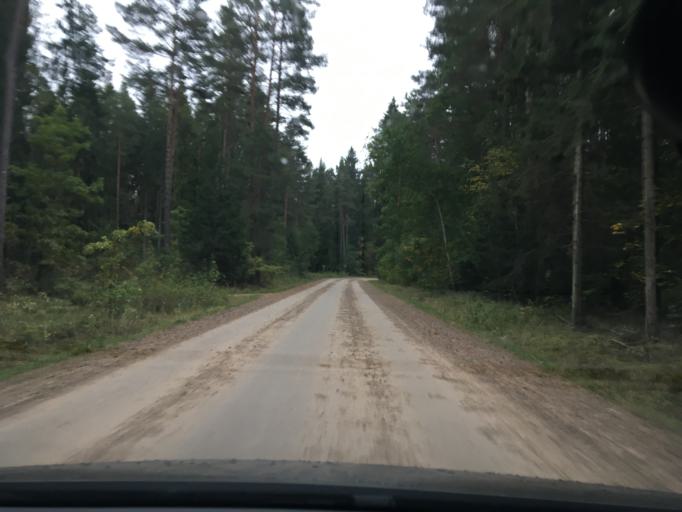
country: LV
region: Kuldigas Rajons
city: Kuldiga
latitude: 56.9866
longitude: 21.9754
